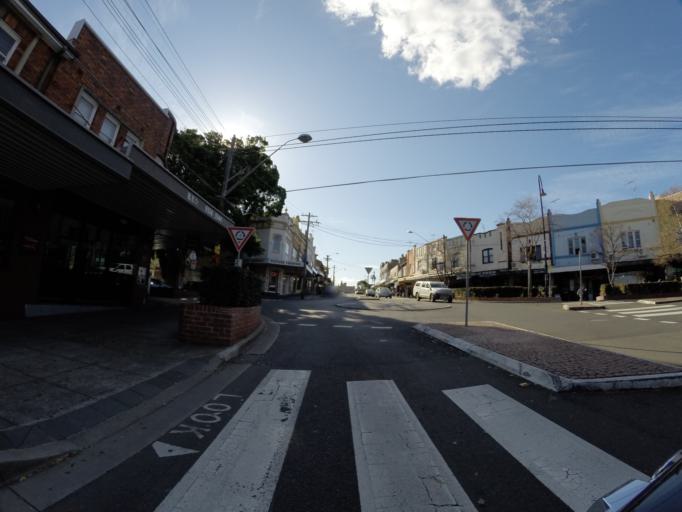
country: AU
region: New South Wales
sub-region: Randwick
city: Randwick
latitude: -33.9204
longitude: 151.2427
